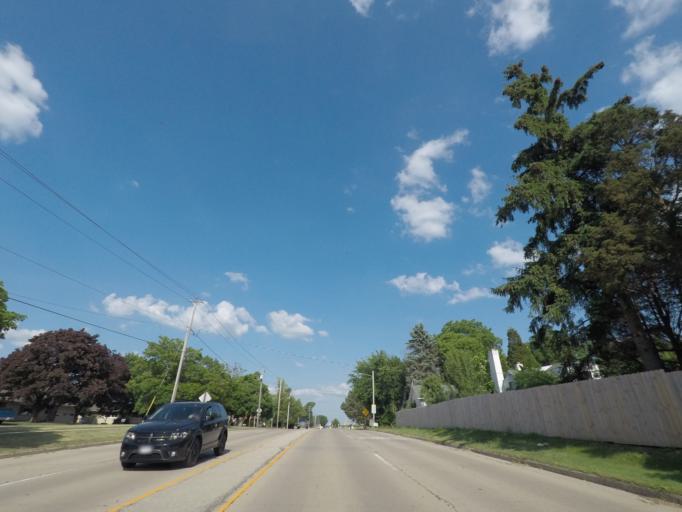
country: US
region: Wisconsin
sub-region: Walworth County
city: East Troy
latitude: 42.7923
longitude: -88.3992
